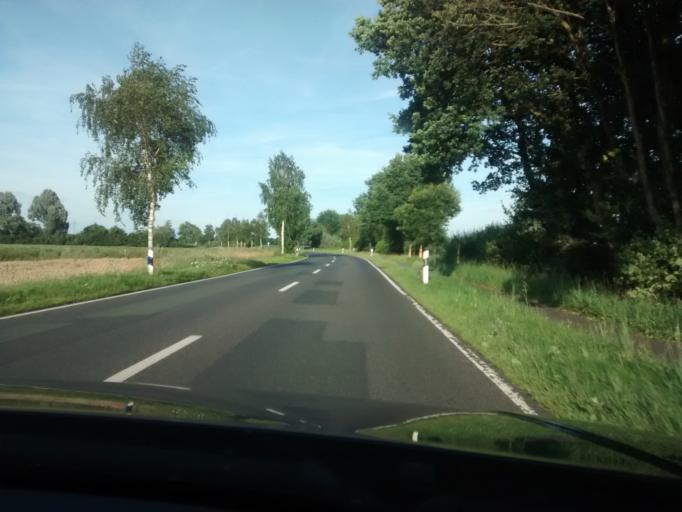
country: DE
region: Lower Saxony
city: Meppen
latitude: 52.6683
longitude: 7.2169
